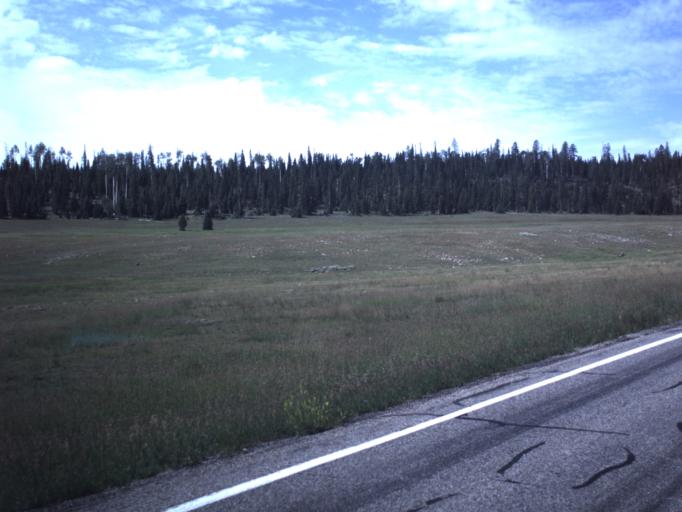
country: US
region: Utah
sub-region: Iron County
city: Cedar City
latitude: 37.5708
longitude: -112.8119
